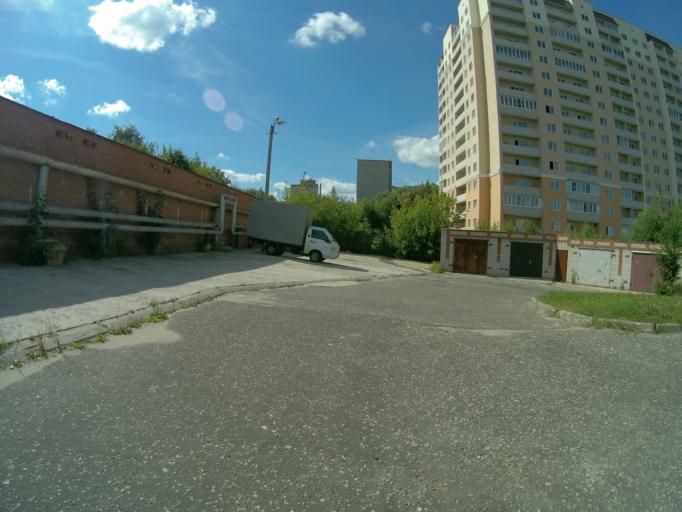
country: RU
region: Vladimir
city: Vladimir
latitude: 56.1365
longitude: 40.3734
